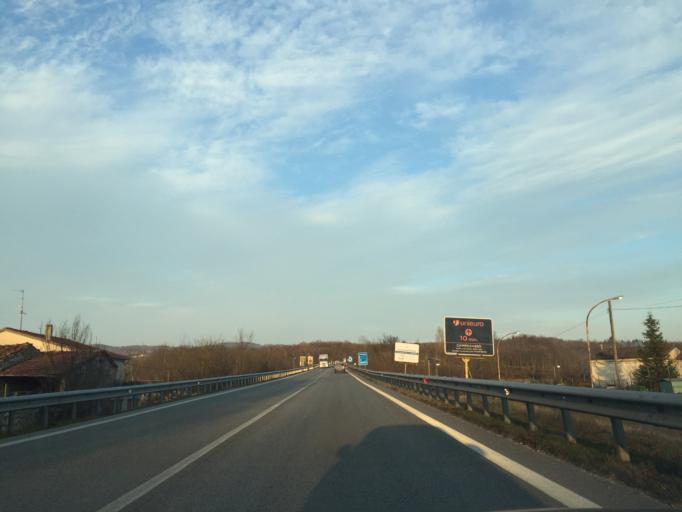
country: IT
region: Molise
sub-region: Provincia di Campobasso
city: Vinchiaturo
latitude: 41.4802
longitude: 14.5824
